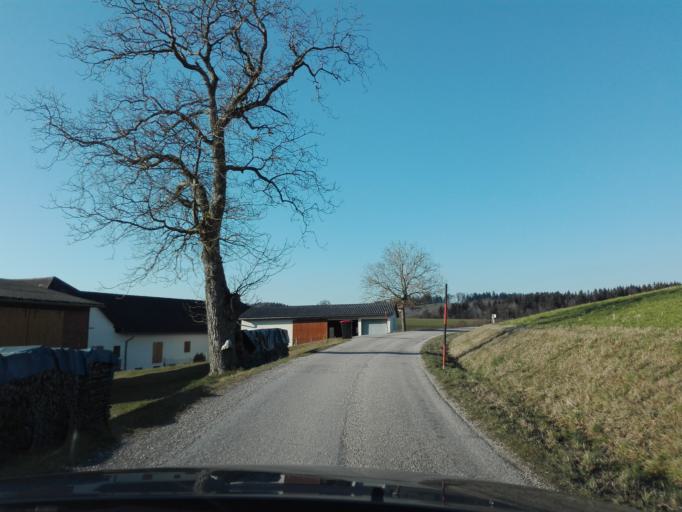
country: AT
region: Upper Austria
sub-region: Politischer Bezirk Rohrbach
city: Kleinzell im Muehlkreis
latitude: 48.3888
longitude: 13.9509
